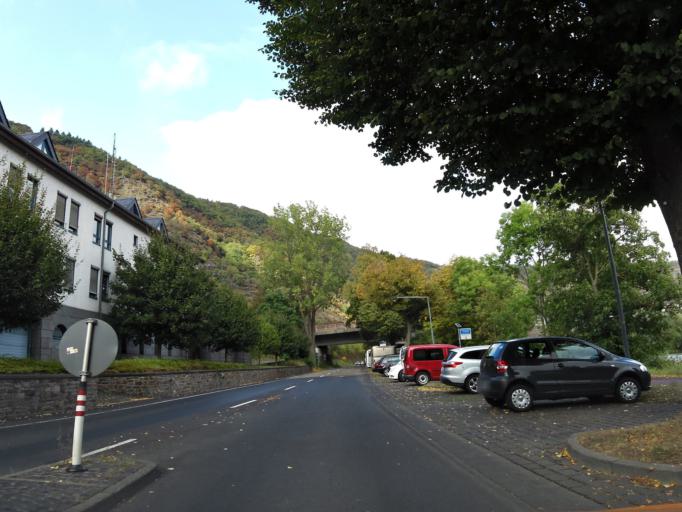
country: DE
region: Rheinland-Pfalz
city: Cochem
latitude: 50.1539
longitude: 7.1683
